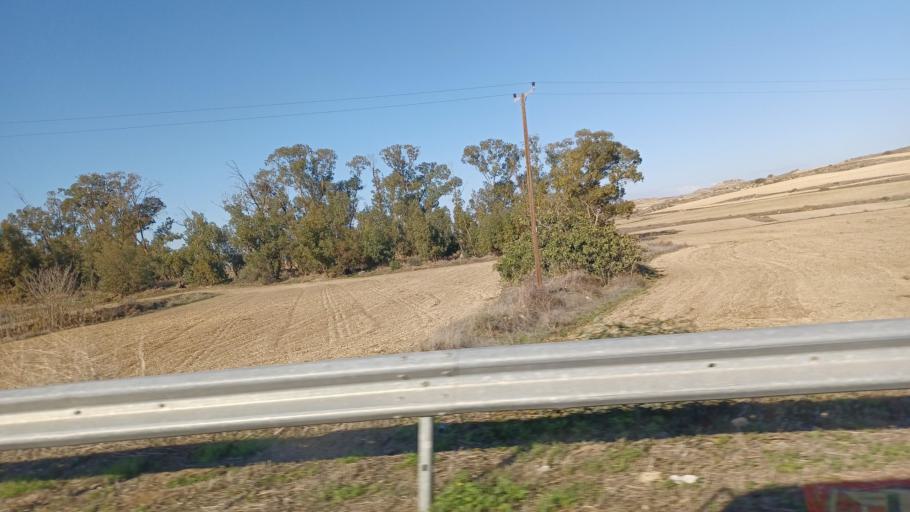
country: CY
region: Lefkosia
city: Lympia
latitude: 35.0353
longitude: 33.4932
